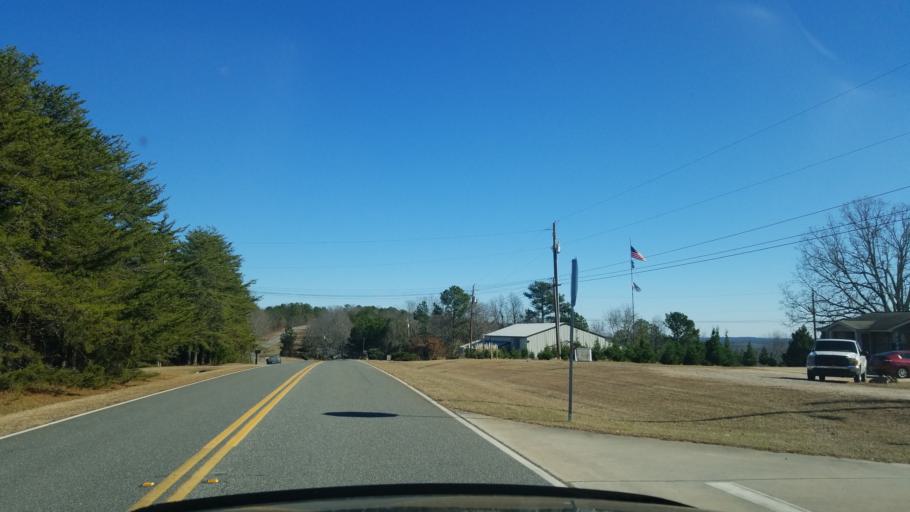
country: US
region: Georgia
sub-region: Meriwether County
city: Manchester
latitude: 32.8426
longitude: -84.6651
